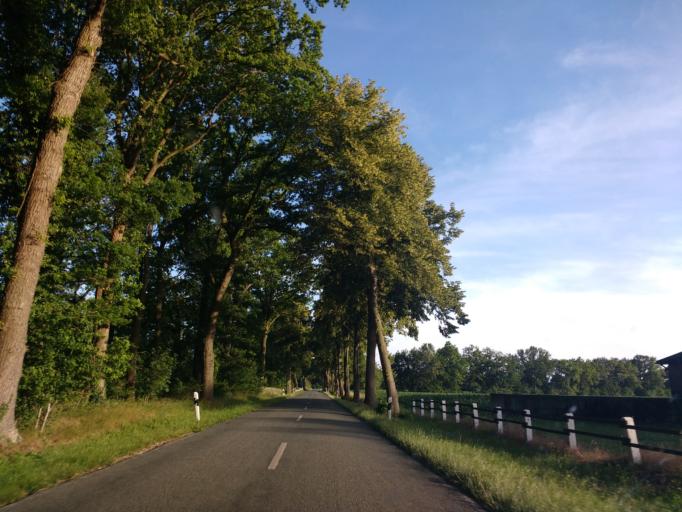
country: DE
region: North Rhine-Westphalia
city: Rietberg
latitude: 51.7221
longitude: 8.4397
